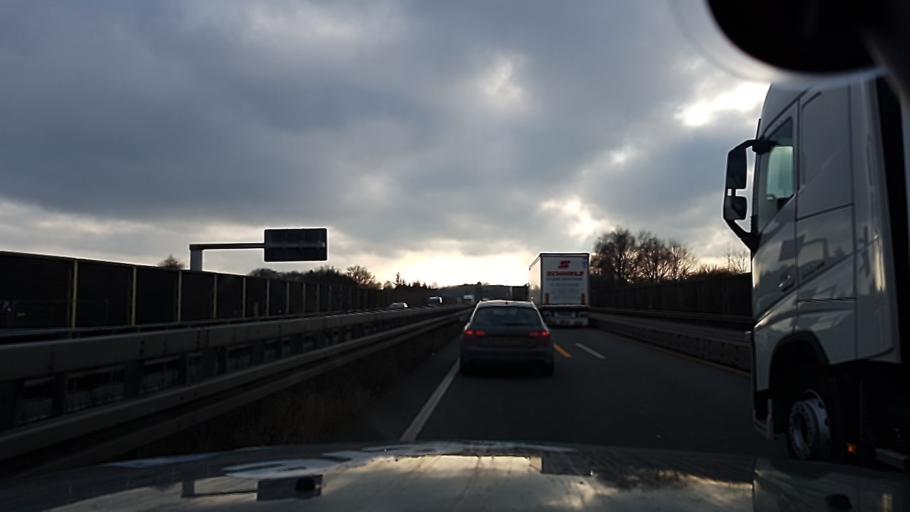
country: DE
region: North Rhine-Westphalia
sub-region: Regierungsbezirk Munster
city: Lotte
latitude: 52.2945
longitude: 7.9412
